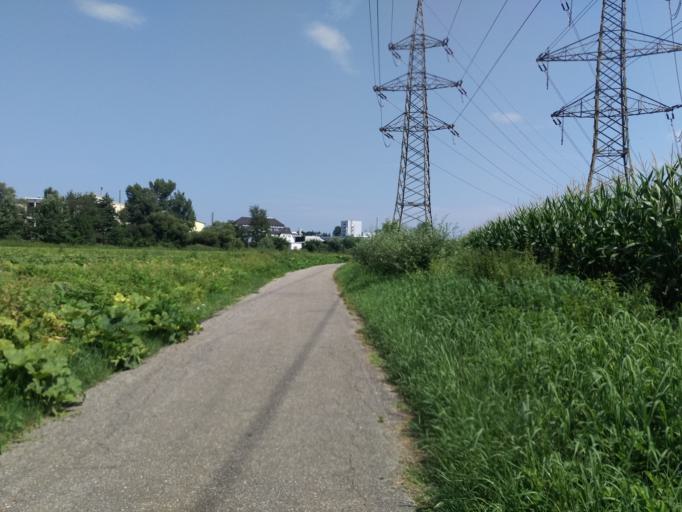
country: AT
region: Styria
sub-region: Politischer Bezirk Graz-Umgebung
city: Werndorf
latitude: 46.9140
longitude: 15.4835
